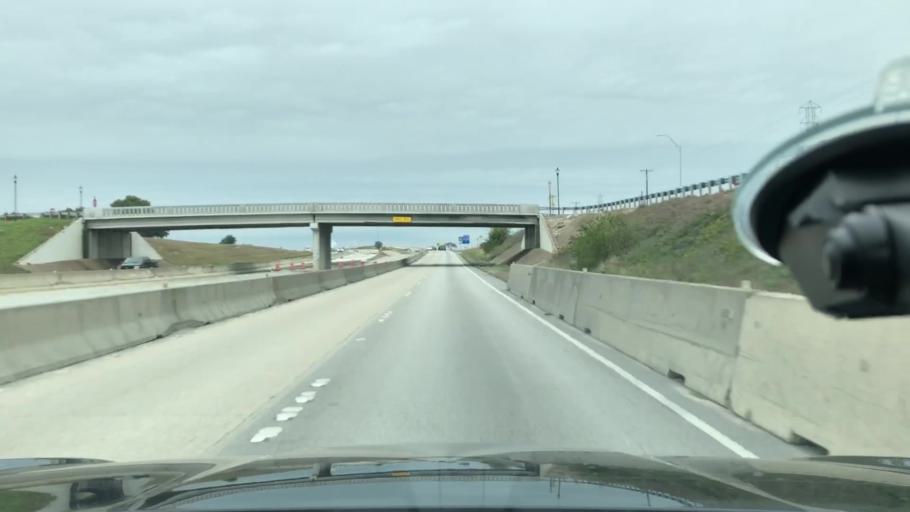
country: US
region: Texas
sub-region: Ellis County
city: Waxahachie
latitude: 32.3565
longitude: -96.8546
